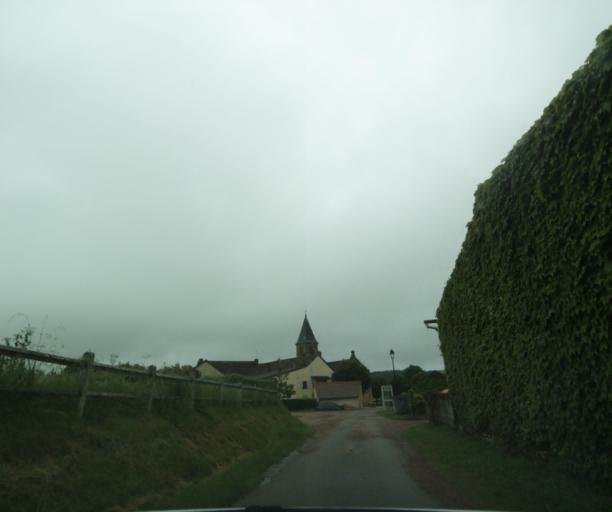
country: FR
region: Bourgogne
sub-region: Departement de Saone-et-Loire
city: Charolles
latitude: 46.4701
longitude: 4.2434
